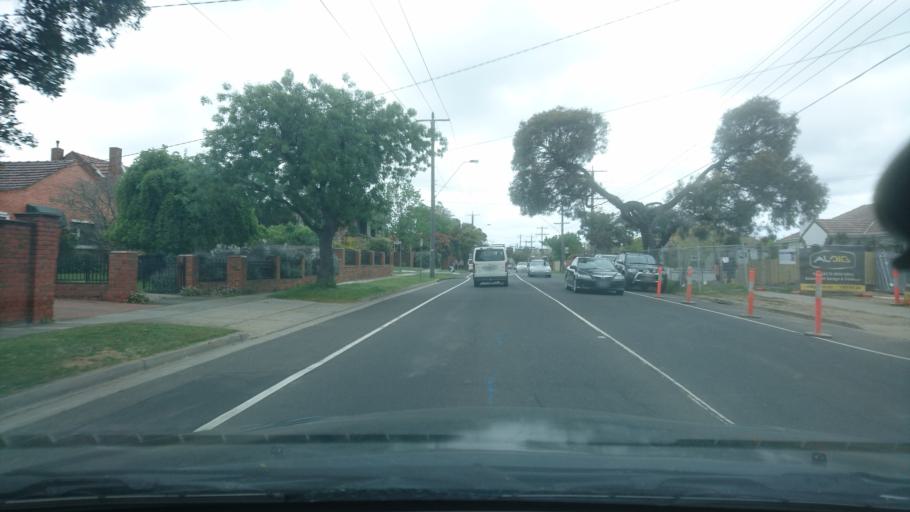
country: AU
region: Victoria
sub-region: Glen Eira
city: Murrumbeena
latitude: -37.8892
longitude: 145.0778
